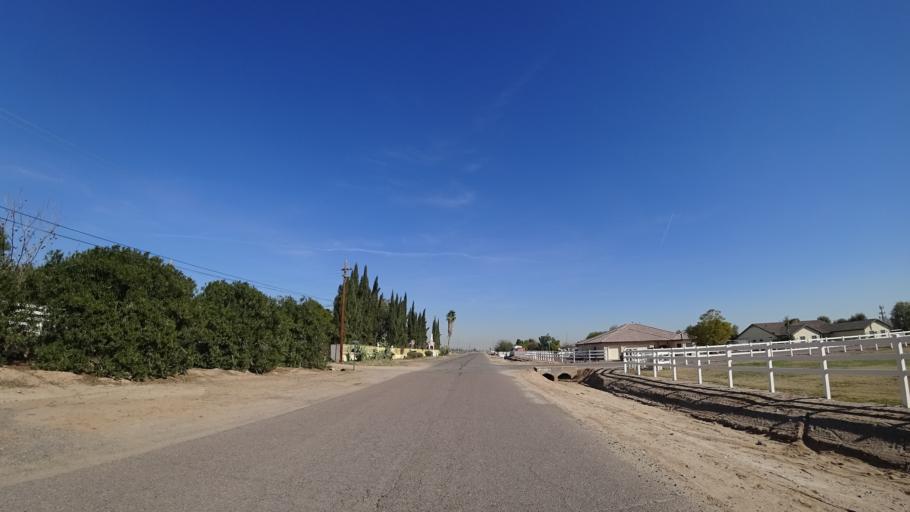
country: US
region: Arizona
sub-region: Maricopa County
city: Citrus Park
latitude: 33.5300
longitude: -112.4307
